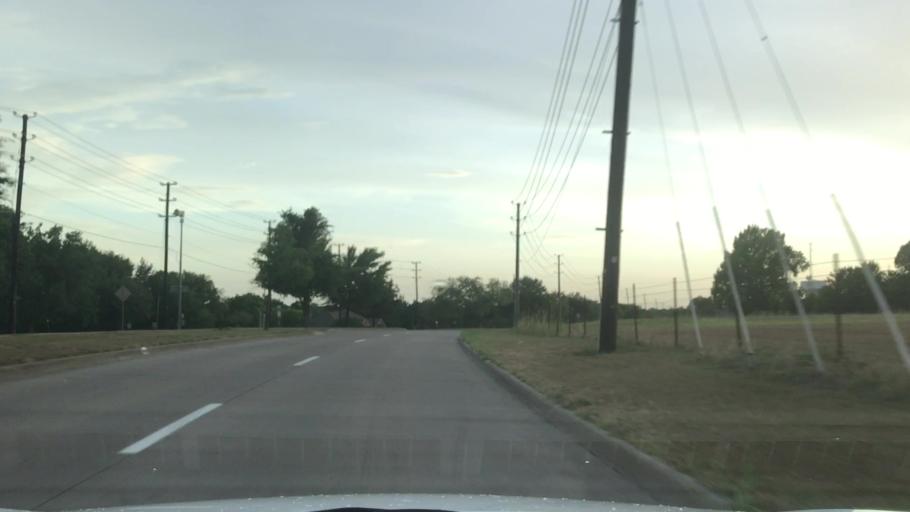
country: US
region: Texas
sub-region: Dallas County
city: Balch Springs
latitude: 32.7087
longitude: -96.5574
